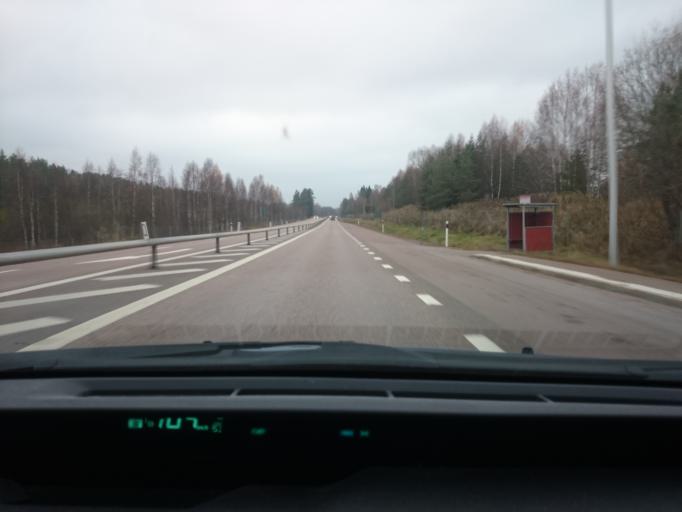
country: SE
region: Dalarna
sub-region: Avesta Kommun
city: Avesta
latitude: 60.1627
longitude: 16.1592
